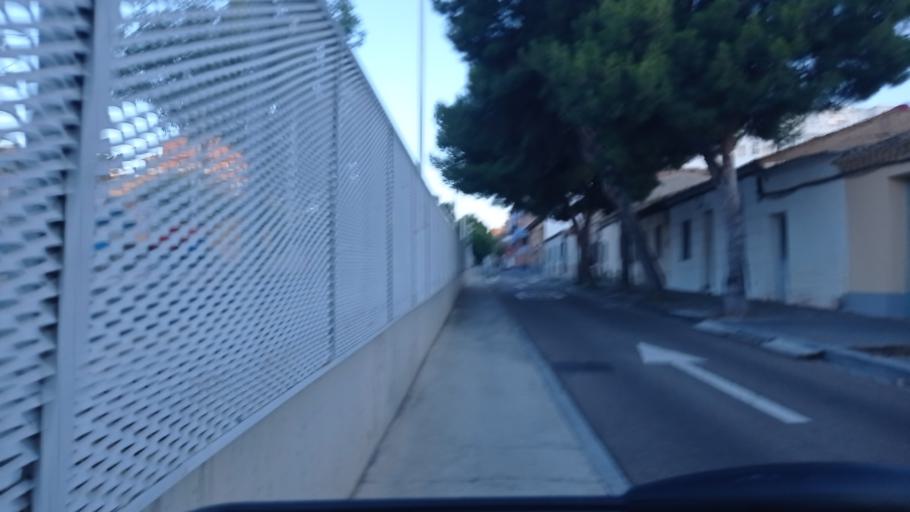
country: ES
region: Aragon
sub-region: Provincia de Zaragoza
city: Oliver-Valdefierro, Oliver, Valdefierro
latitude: 41.6548
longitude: -0.9247
